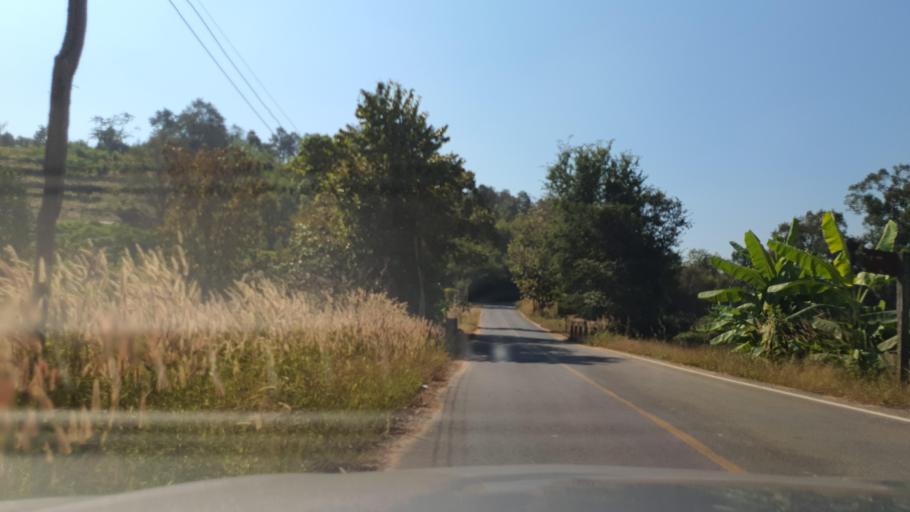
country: TH
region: Nan
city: Pua
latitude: 19.1130
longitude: 100.9092
